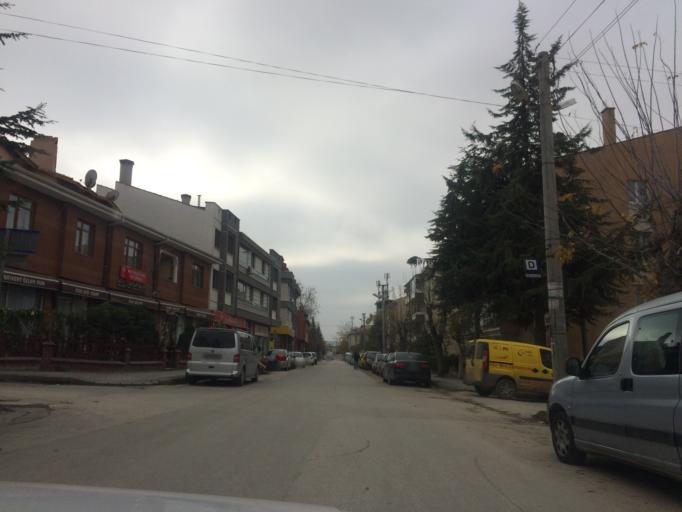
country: TR
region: Eskisehir
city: Eskisehir
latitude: 39.7797
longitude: 30.4825
